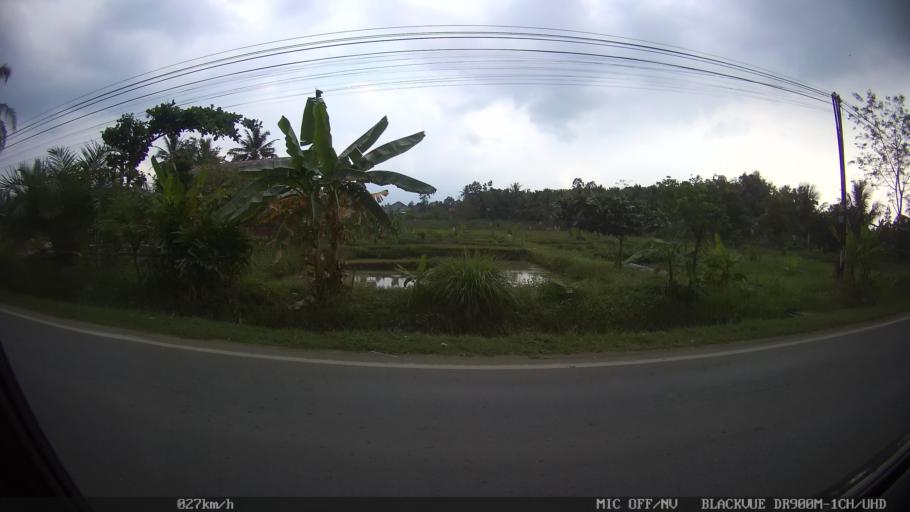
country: ID
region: Lampung
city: Gedongtataan
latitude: -5.3757
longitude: 105.0896
